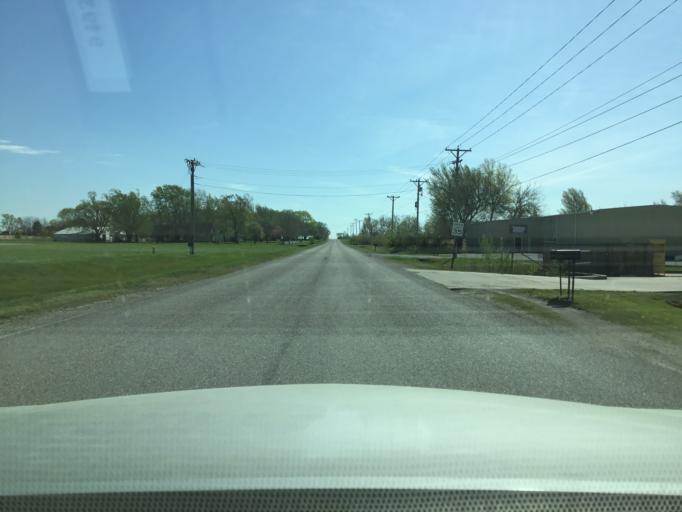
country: US
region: Kansas
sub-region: Neosho County
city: Chanute
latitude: 37.6458
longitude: -95.4521
